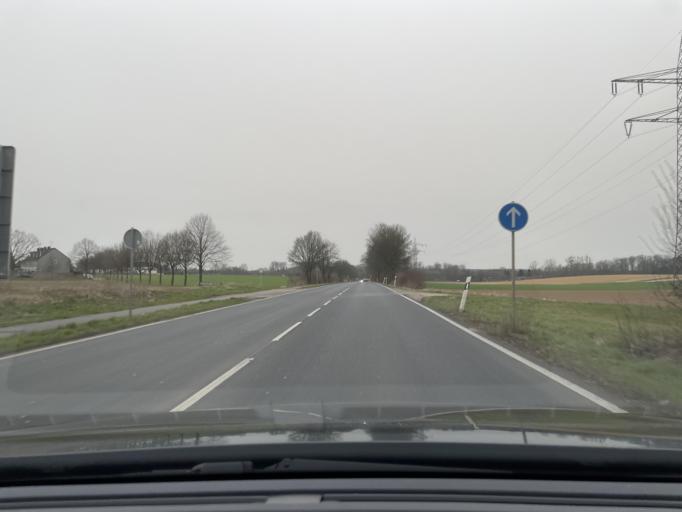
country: DE
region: North Rhine-Westphalia
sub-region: Regierungsbezirk Dusseldorf
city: Monchengladbach
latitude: 51.1186
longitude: 6.4243
